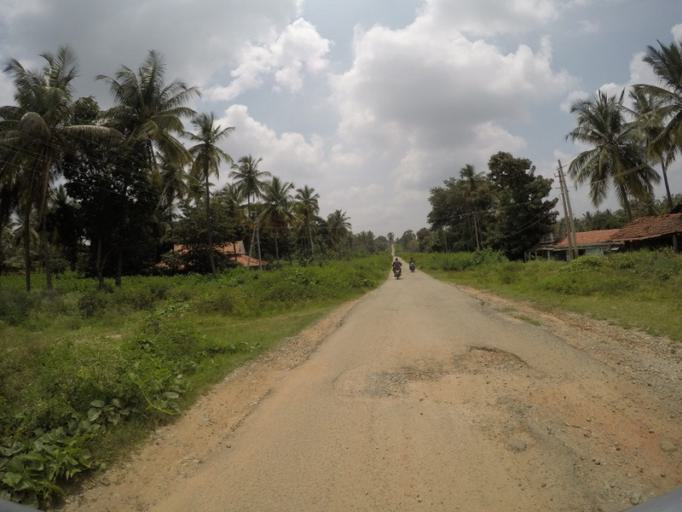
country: IN
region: Karnataka
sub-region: Ramanagara
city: Kanakapura
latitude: 12.7081
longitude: 77.4740
